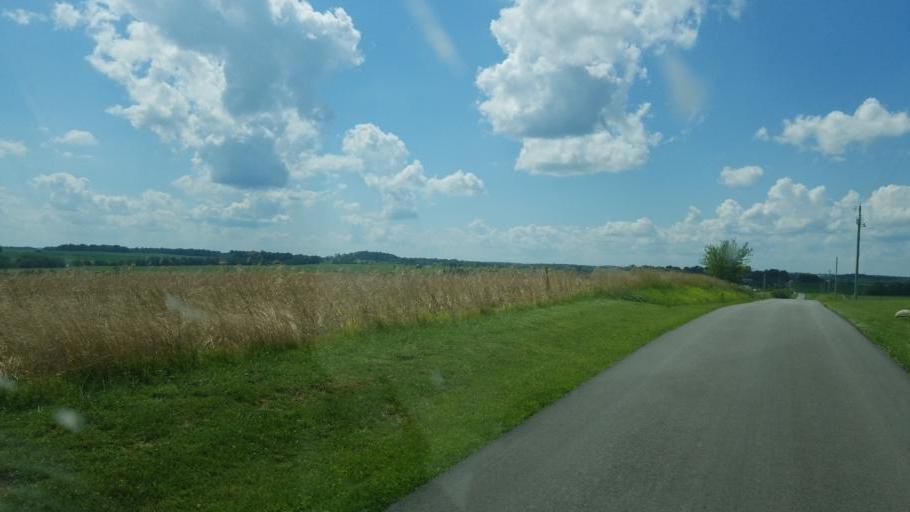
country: US
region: Ohio
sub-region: Highland County
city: Greenfield
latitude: 39.2547
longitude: -83.4303
